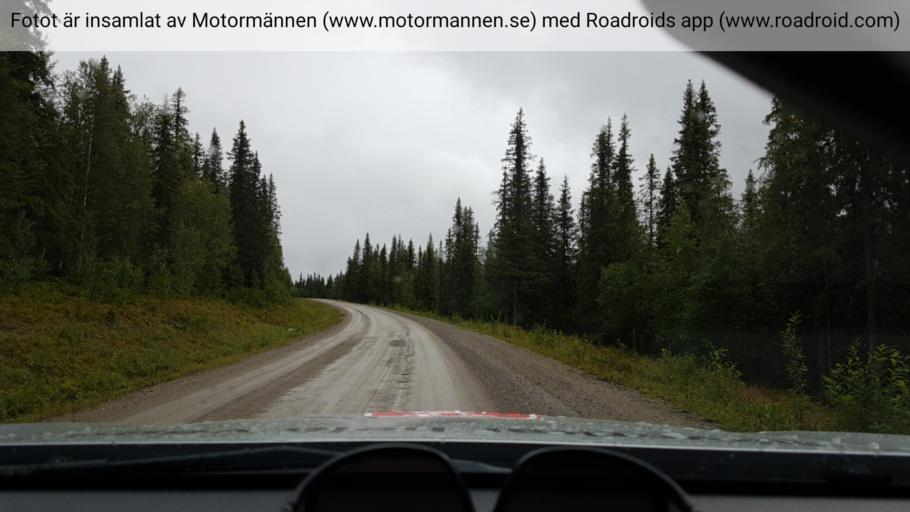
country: SE
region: Vaesterbotten
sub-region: Storumans Kommun
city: Storuman
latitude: 64.9228
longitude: 17.2549
